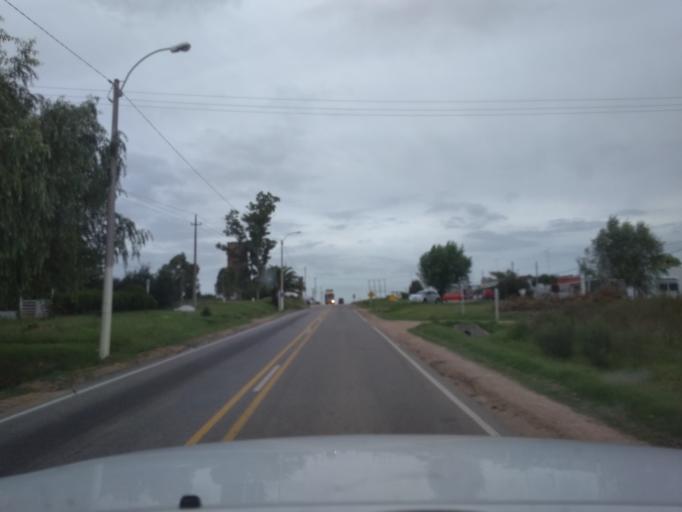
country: UY
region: Canelones
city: Tala
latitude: -34.3491
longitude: -55.7669
